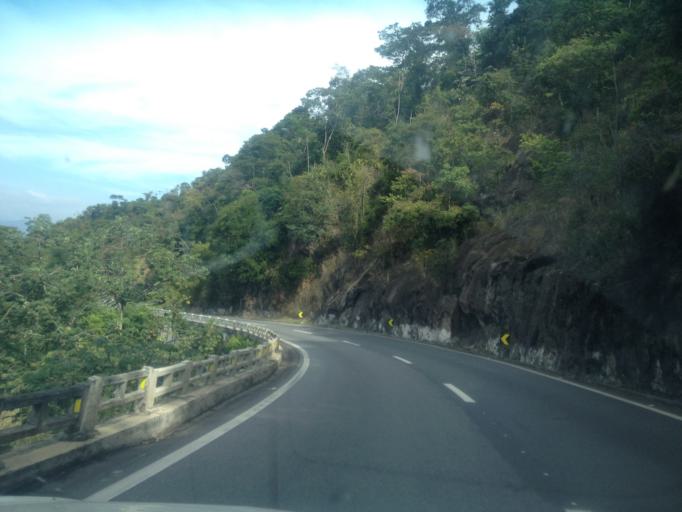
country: BR
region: Rio de Janeiro
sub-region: Pirai
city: Pirai
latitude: -22.6698
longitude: -43.8275
